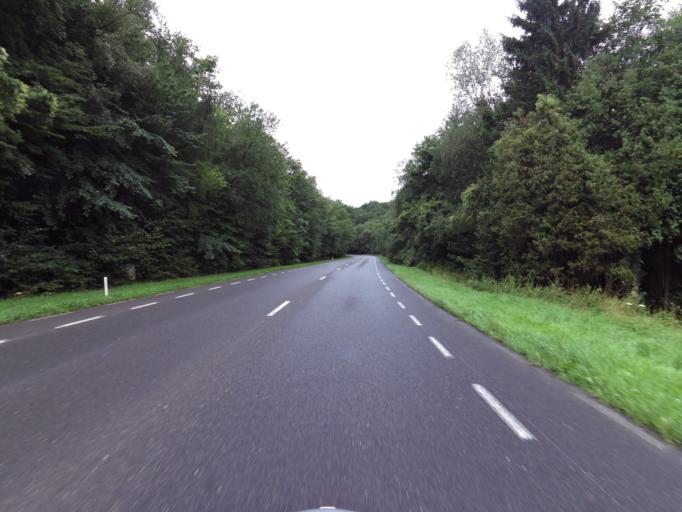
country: BE
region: Wallonia
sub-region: Province du Luxembourg
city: Tellin
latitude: 50.1171
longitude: 5.1736
